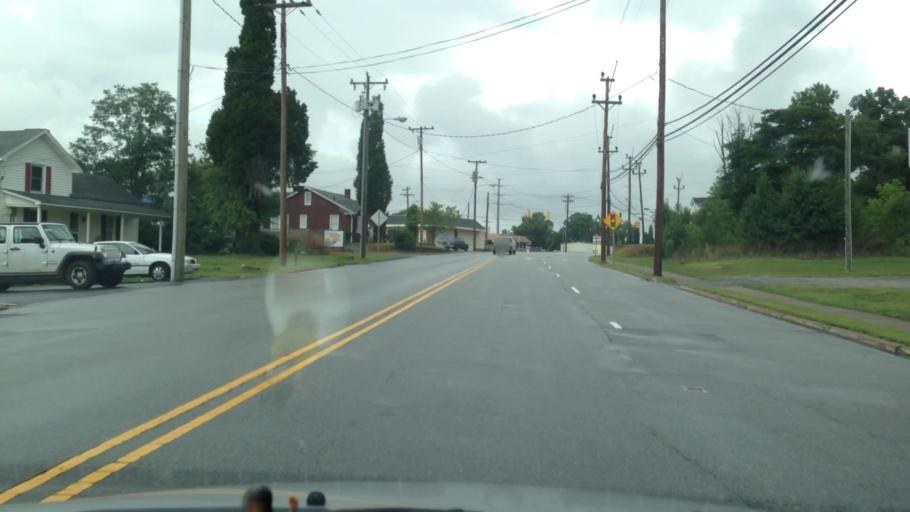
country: US
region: North Carolina
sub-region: Rockingham County
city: Madison
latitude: 36.3906
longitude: -79.9682
